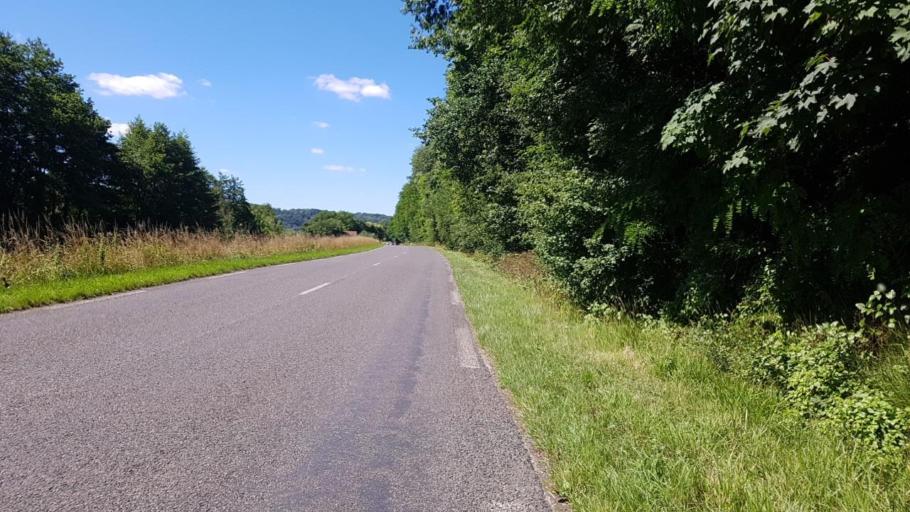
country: FR
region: Ile-de-France
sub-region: Departement de Seine-et-Marne
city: Saacy-sur-Marne
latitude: 48.9715
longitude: 3.2087
